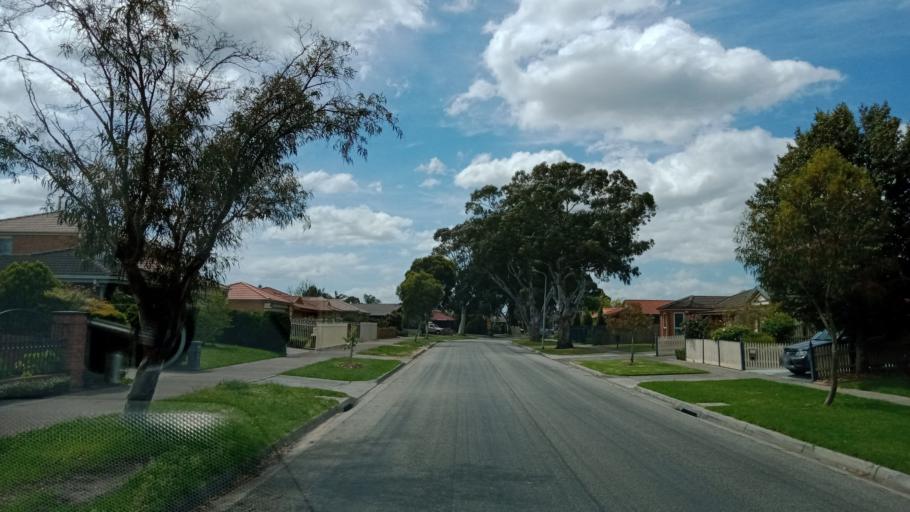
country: AU
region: Victoria
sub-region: Kingston
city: Patterson Lakes
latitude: -38.0521
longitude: 145.1392
